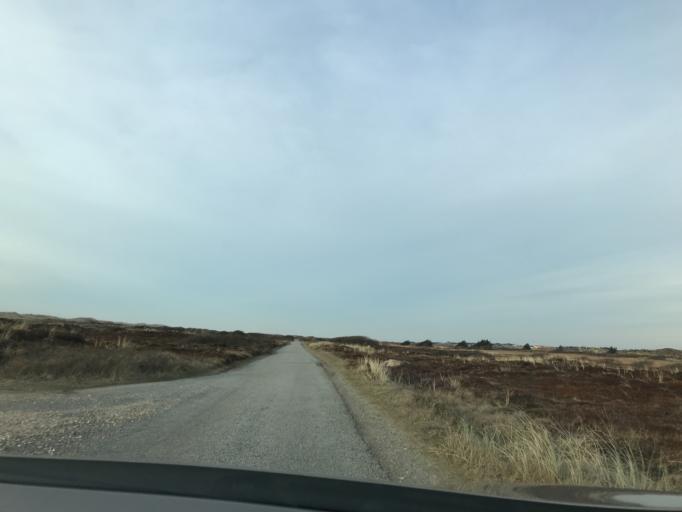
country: DK
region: South Denmark
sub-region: Varde Kommune
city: Oksbol
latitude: 55.8004
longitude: 8.1817
